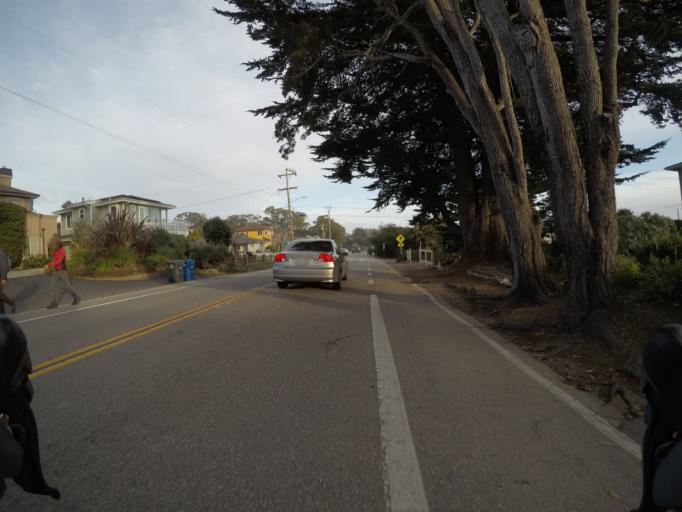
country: US
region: California
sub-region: Santa Cruz County
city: Twin Lakes
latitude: 36.9612
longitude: -121.9866
